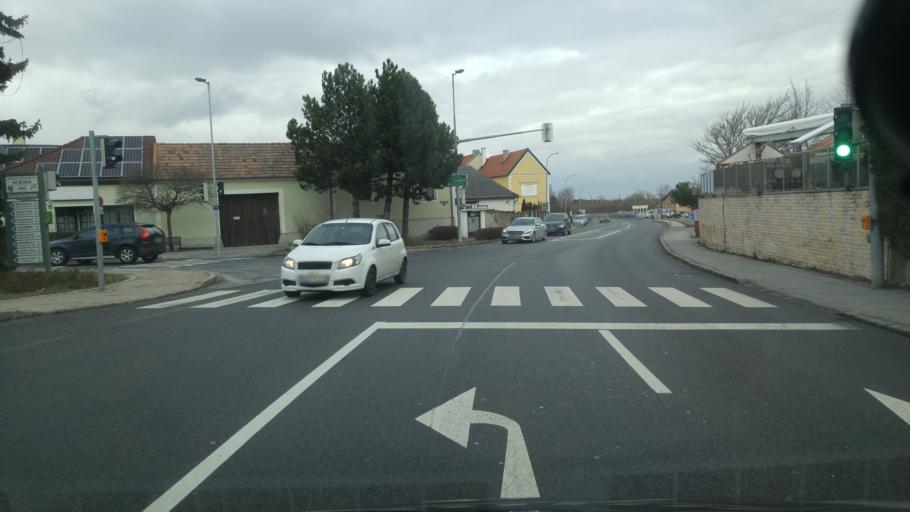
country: AT
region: Lower Austria
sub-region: Politischer Bezirk Baden
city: Bad Voslau
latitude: 47.9840
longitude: 16.2214
